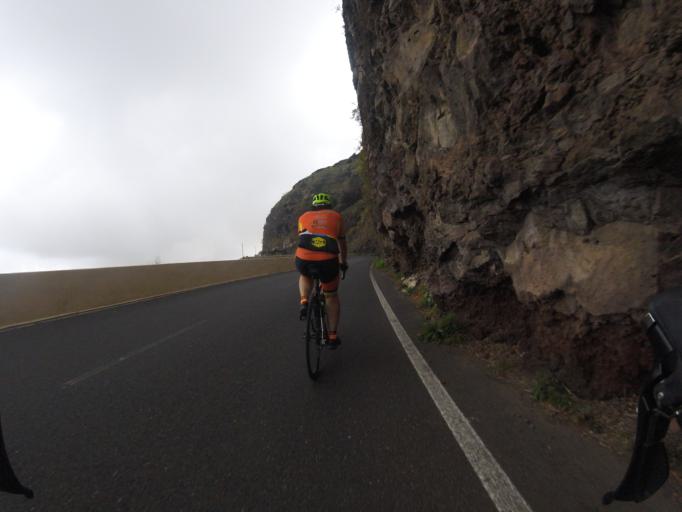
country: ES
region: Canary Islands
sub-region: Provincia de Santa Cruz de Tenerife
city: Guimar
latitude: 28.2937
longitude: -16.4059
